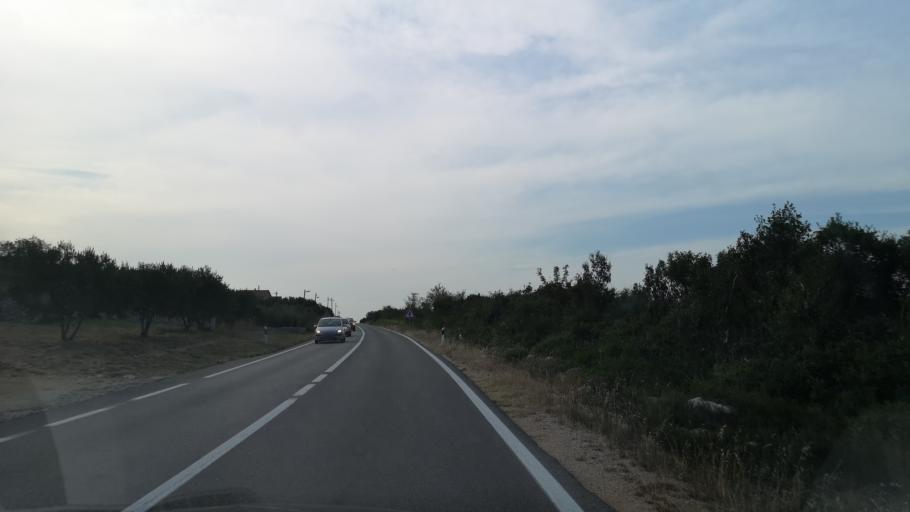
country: HR
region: Sibensko-Kniniska
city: Zaton
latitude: 43.8528
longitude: 15.7634
